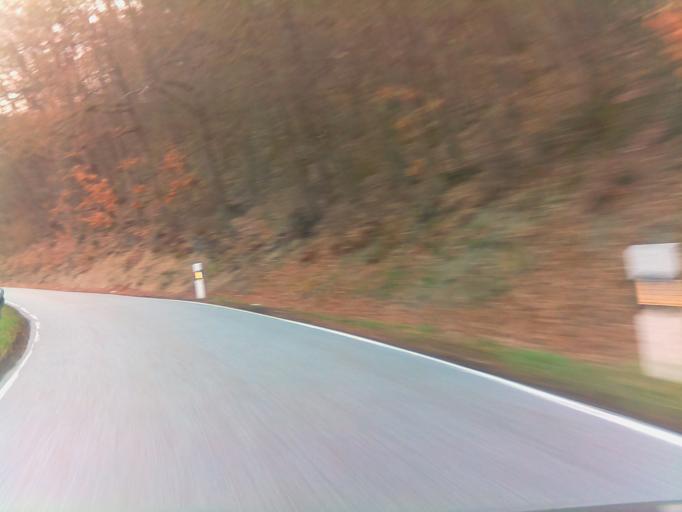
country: DE
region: Rheinland-Pfalz
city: Sankt Julian
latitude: 49.6192
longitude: 7.5102
